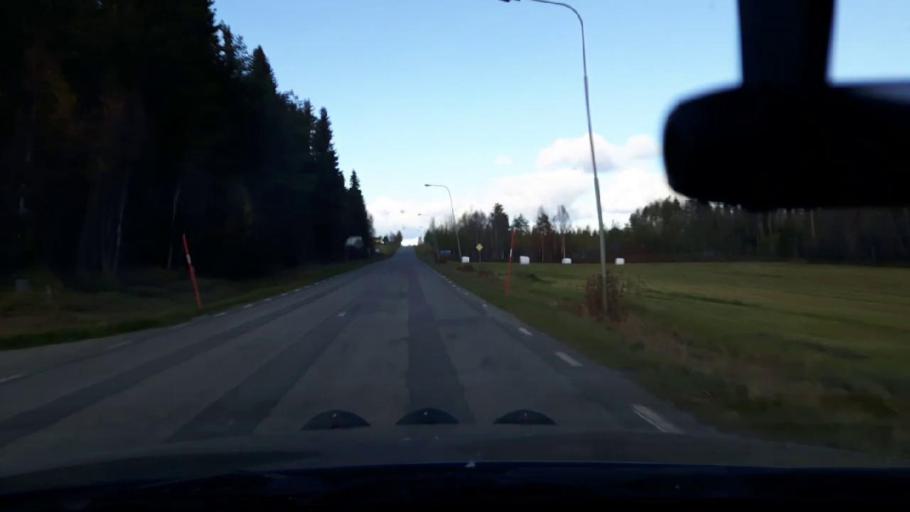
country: SE
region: Jaemtland
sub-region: Bergs Kommun
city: Hoverberg
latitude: 63.0017
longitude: 14.3399
